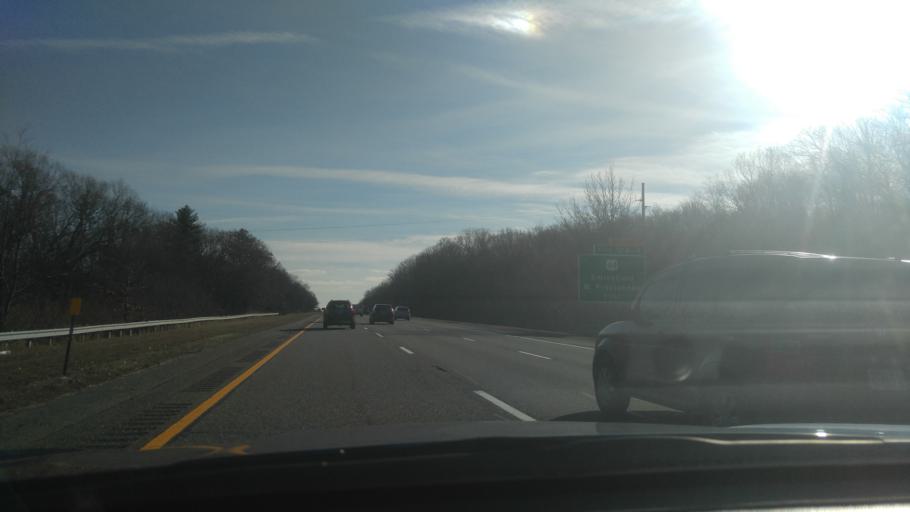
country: US
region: Rhode Island
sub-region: Providence County
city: Greenville
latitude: 41.8872
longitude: -71.5205
